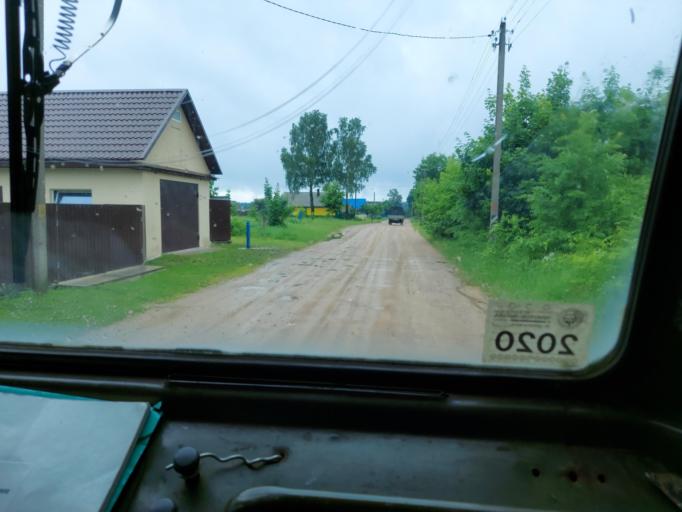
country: BY
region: Mogilev
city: Poselok Voskhod
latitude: 53.6814
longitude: 30.3879
